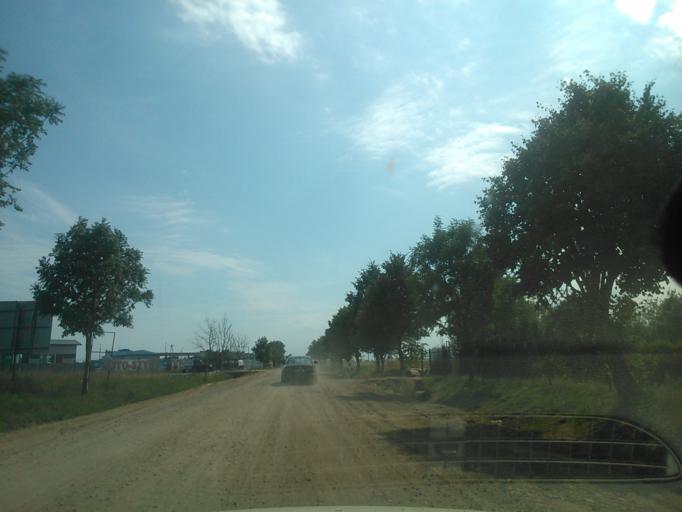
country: PL
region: Warmian-Masurian Voivodeship
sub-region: Powiat dzialdowski
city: Dzialdowo
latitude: 53.2252
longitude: 20.2011
